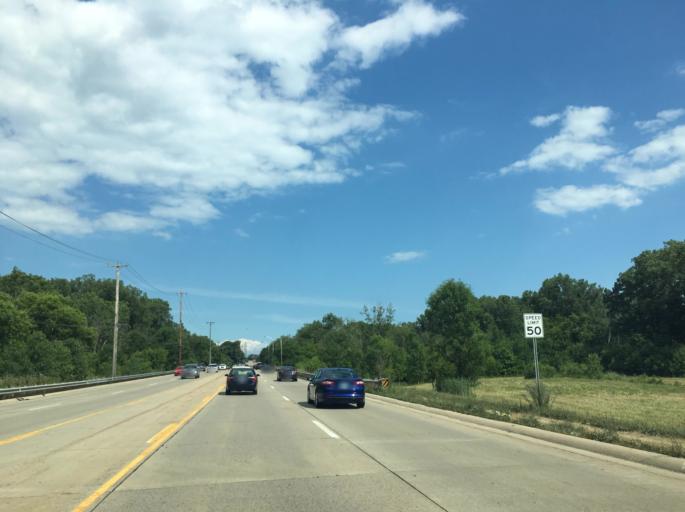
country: US
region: Michigan
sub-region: Macomb County
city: Clinton
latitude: 42.6024
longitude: -82.9127
